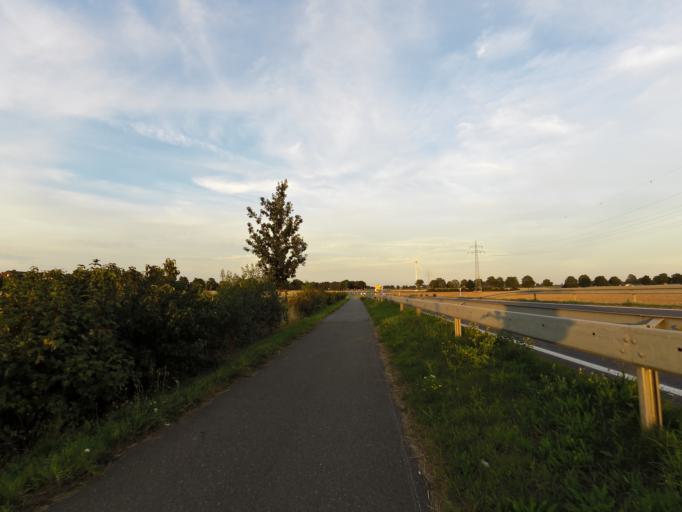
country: DE
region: North Rhine-Westphalia
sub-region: Regierungsbezirk Dusseldorf
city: Kleve
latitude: 51.8174
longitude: 6.1606
